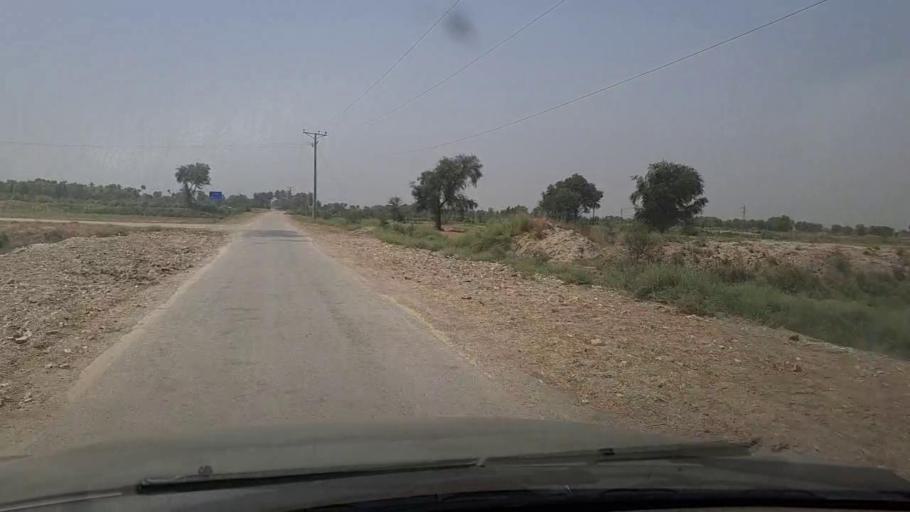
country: PK
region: Sindh
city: Miro Khan
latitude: 27.7749
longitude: 68.1679
